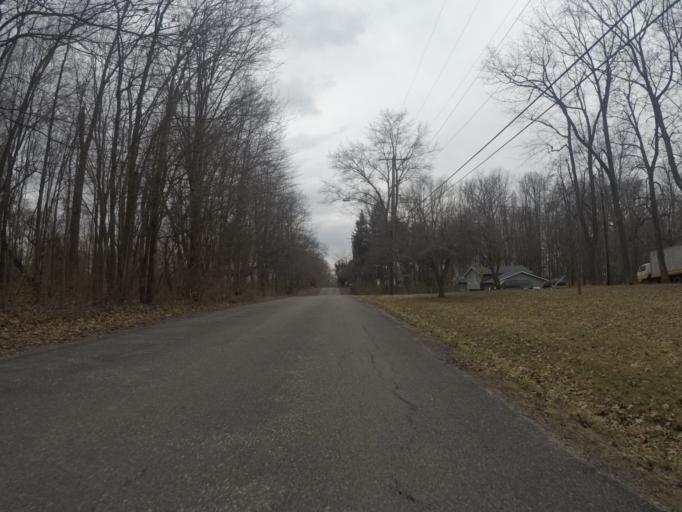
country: US
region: Ohio
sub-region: Portage County
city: Kent
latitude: 41.1609
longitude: -81.3101
